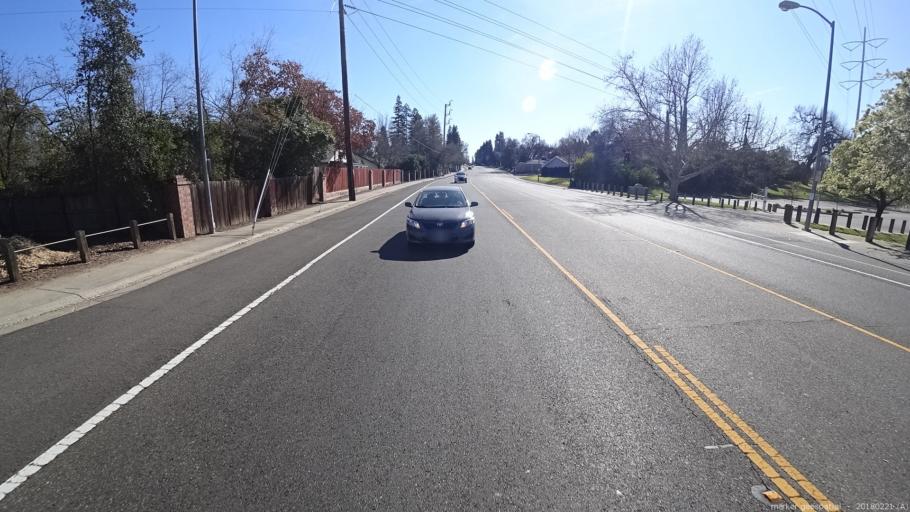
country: US
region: California
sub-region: Sacramento County
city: Citrus Heights
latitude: 38.6880
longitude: -121.2623
